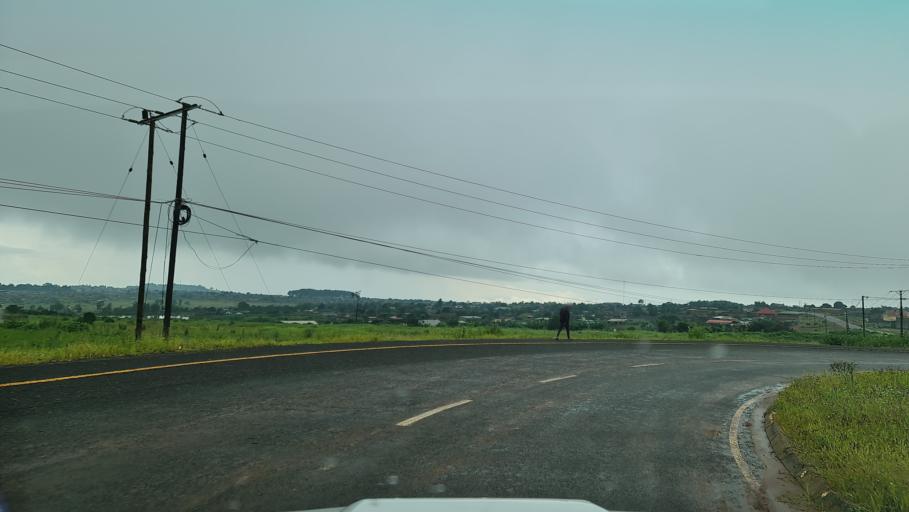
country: MZ
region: Niassa
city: Lichinga
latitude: -13.3370
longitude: 35.2503
